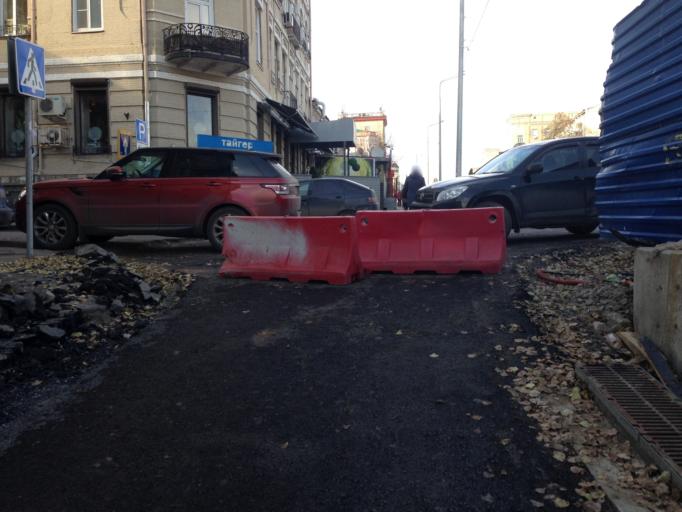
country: RU
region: Rostov
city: Rostov-na-Donu
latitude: 47.2175
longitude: 39.7206
